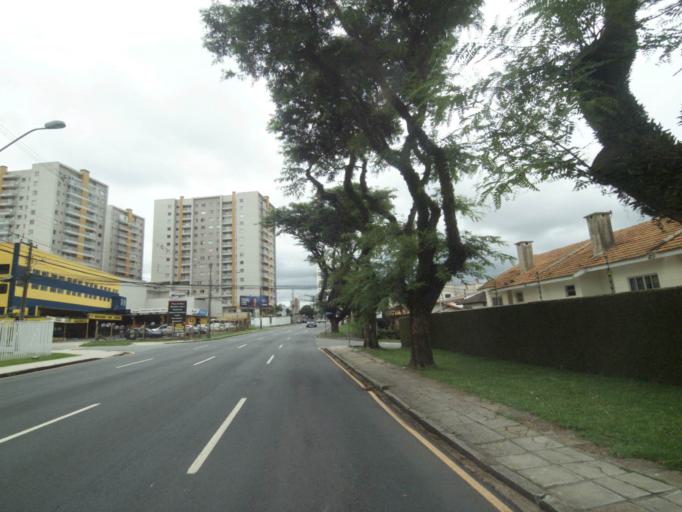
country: BR
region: Parana
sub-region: Curitiba
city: Curitiba
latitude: -25.4997
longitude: -49.2947
